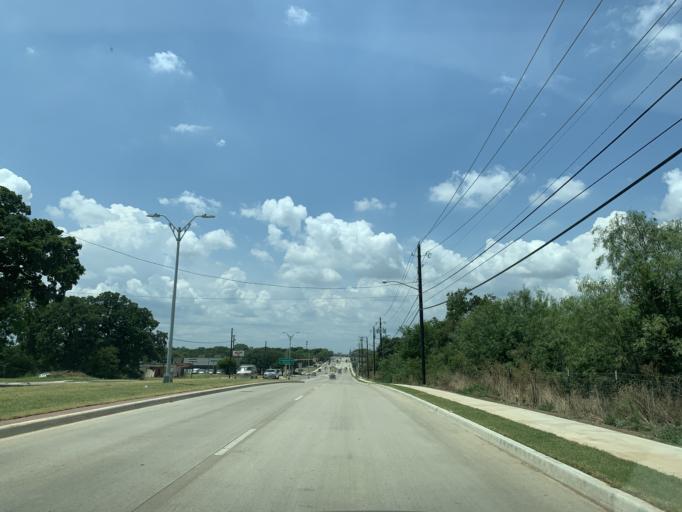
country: US
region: Texas
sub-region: Tarrant County
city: Forest Hill
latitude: 32.7313
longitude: -97.2515
